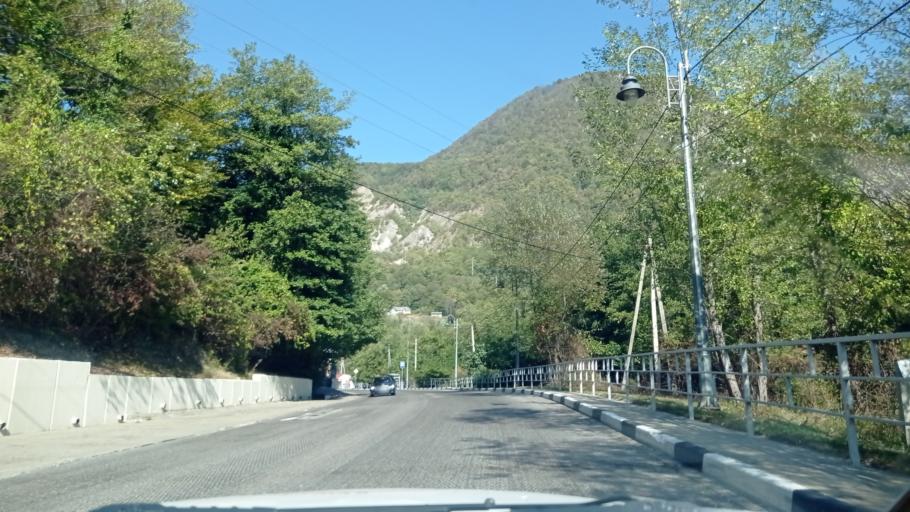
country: RU
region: Krasnodarskiy
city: Vysokoye
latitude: 43.5886
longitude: 40.0076
